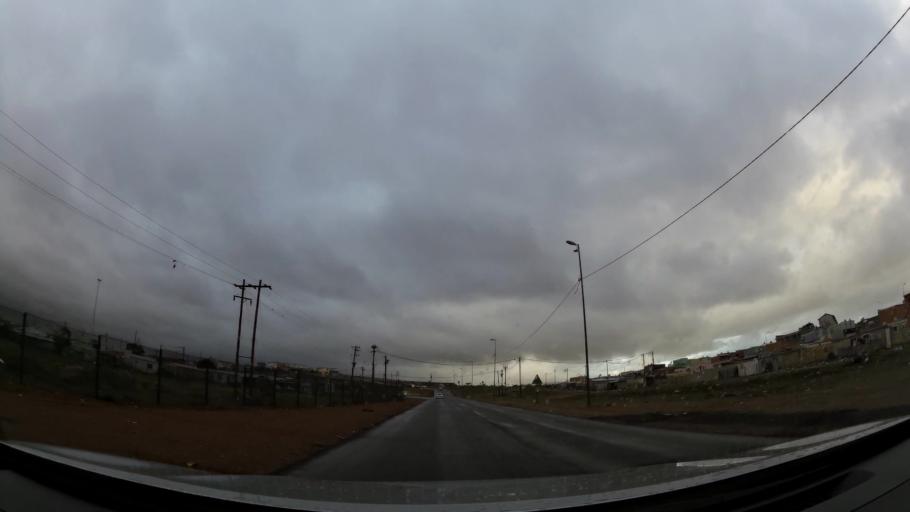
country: ZA
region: Eastern Cape
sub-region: Nelson Mandela Bay Metropolitan Municipality
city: Port Elizabeth
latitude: -33.8880
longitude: 25.5576
